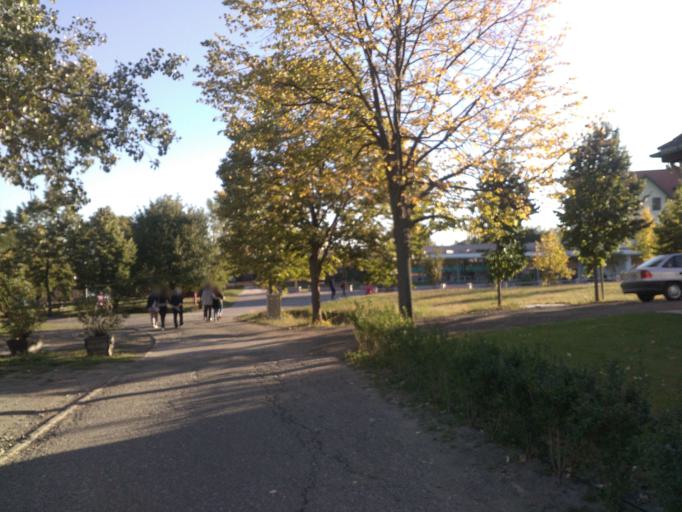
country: HU
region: Pest
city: Szentendre
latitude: 47.6928
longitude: 19.0460
